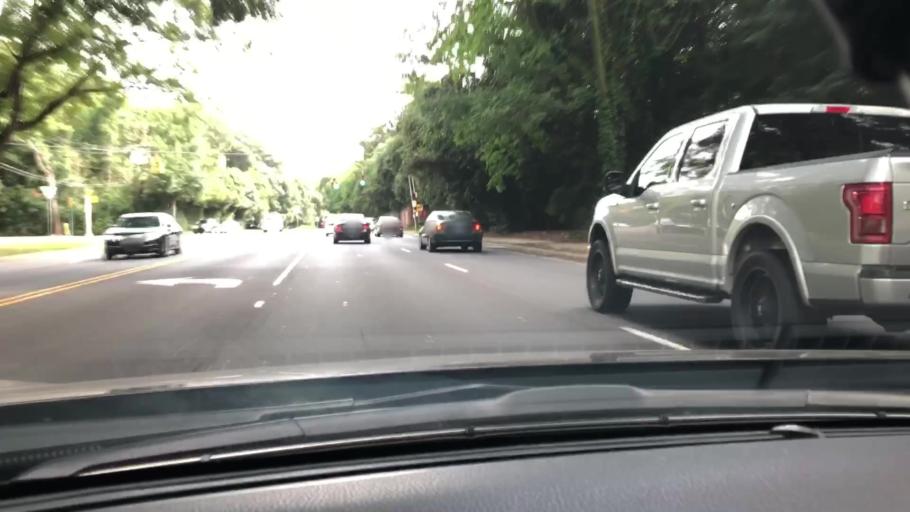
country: US
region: North Carolina
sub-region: Mecklenburg County
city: Charlotte
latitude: 35.1613
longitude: -80.8211
